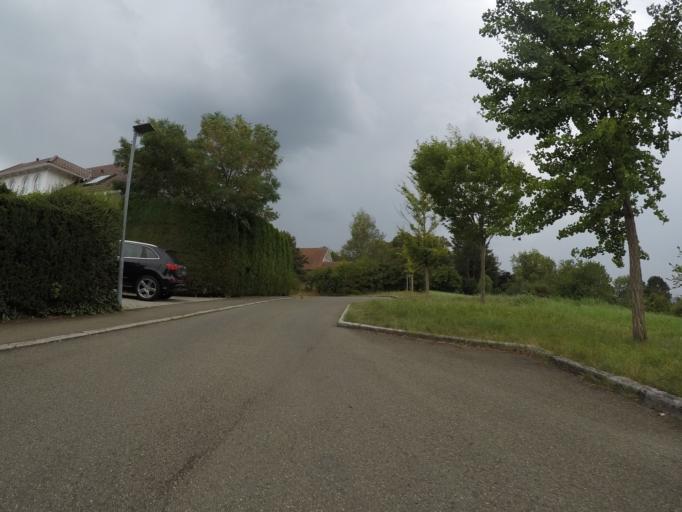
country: DE
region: Baden-Wuerttemberg
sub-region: Tuebingen Region
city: Eningen unter Achalm
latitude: 48.4857
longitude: 9.2429
